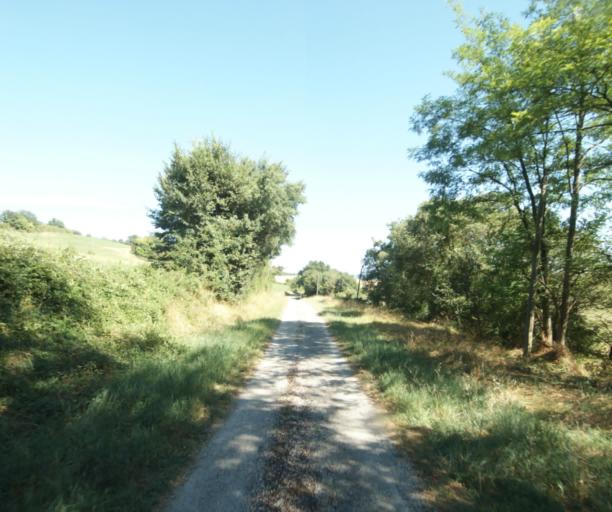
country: FR
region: Midi-Pyrenees
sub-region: Departement de la Haute-Garonne
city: Saint-Felix-Lauragais
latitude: 43.5221
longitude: 1.9051
